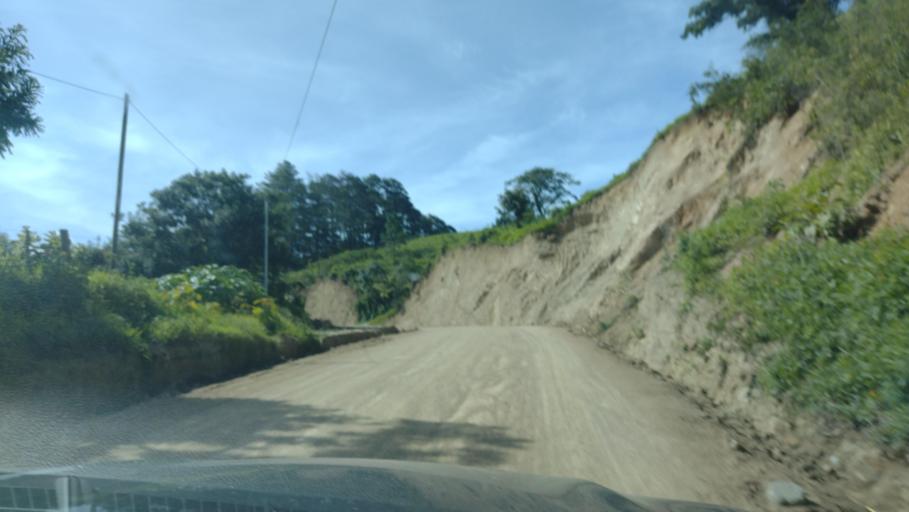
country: GT
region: Guatemala
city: Chinautla
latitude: 14.7542
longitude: -90.5150
